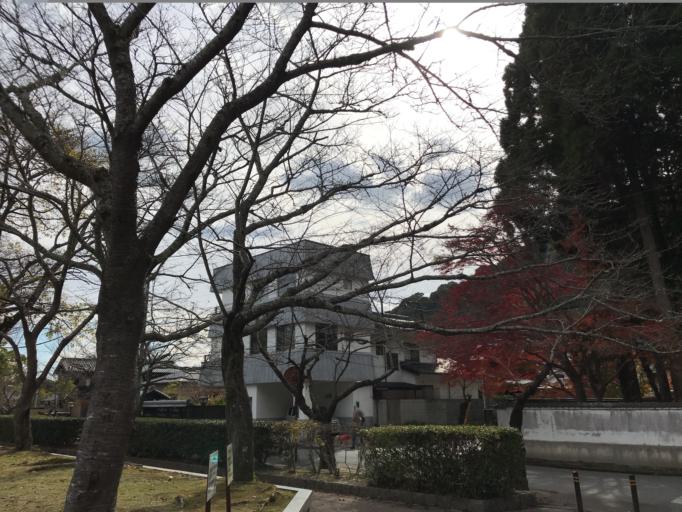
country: JP
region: Yamaguchi
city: Iwakuni
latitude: 34.1696
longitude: 132.1744
